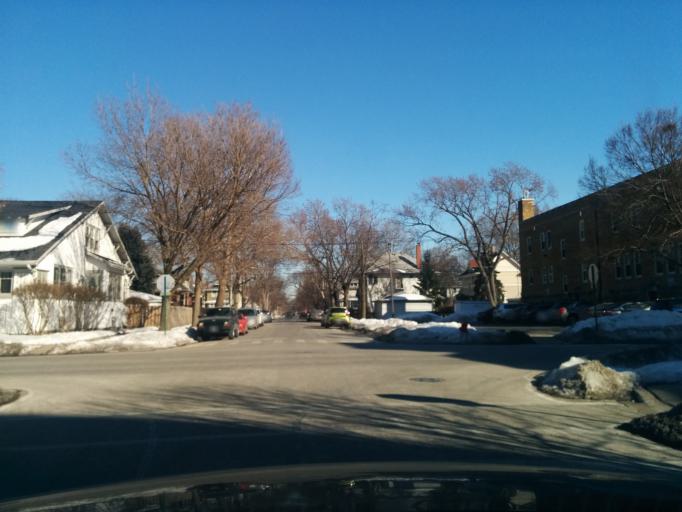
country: US
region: Illinois
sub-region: Cook County
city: Oak Park
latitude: 41.8744
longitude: -87.7894
